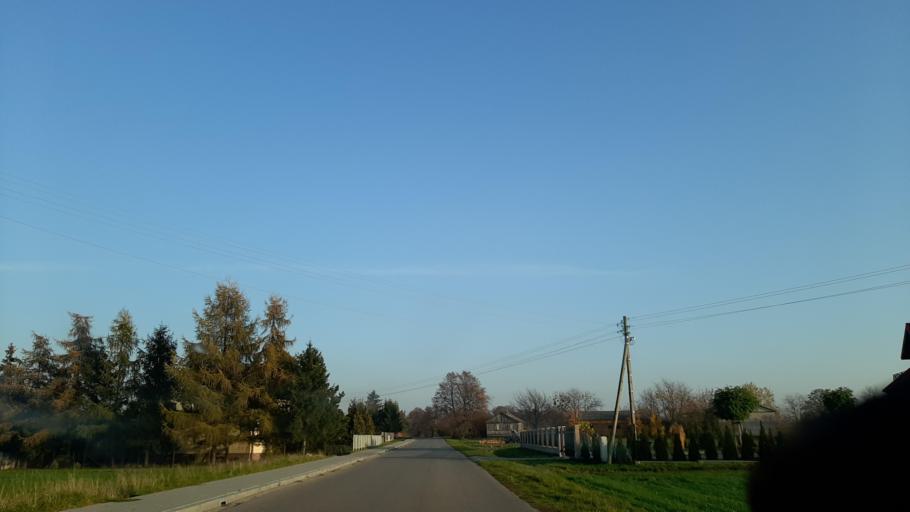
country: PL
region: Lublin Voivodeship
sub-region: Powiat lubelski
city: Garbow
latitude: 51.3845
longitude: 22.3736
